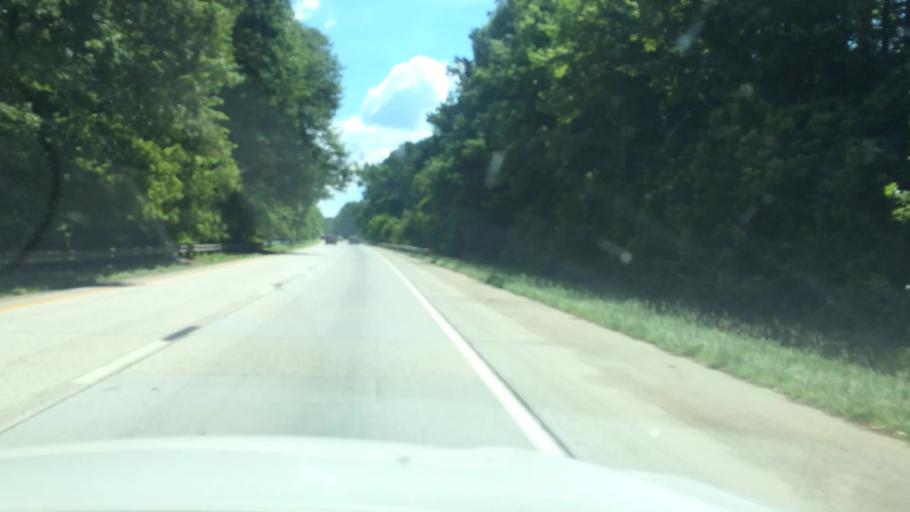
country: US
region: South Carolina
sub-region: Aiken County
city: Belvedere
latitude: 33.5439
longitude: -81.9745
